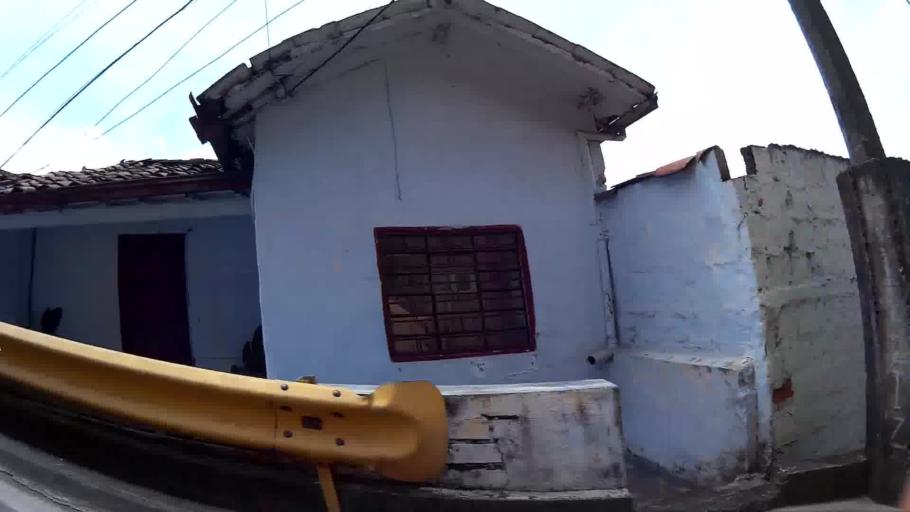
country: CO
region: Antioquia
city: Medellin
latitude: 6.2652
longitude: -75.6264
